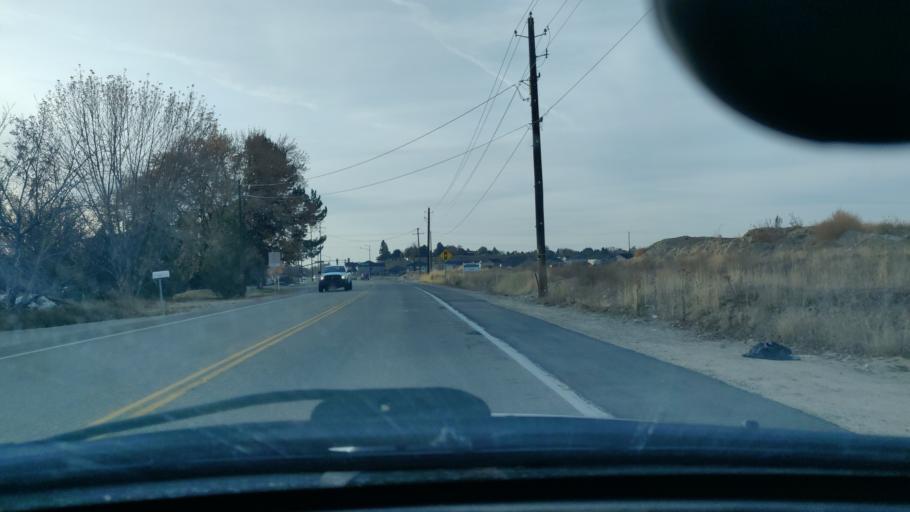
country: US
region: Idaho
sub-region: Ada County
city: Eagle
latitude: 43.6930
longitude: -116.3163
